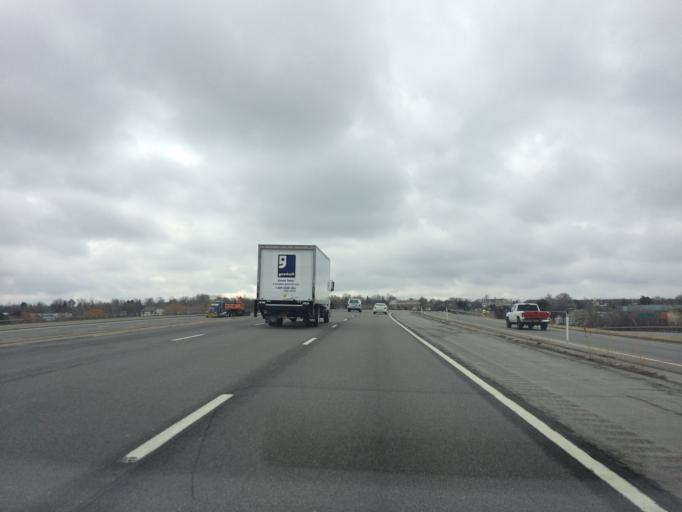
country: US
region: New York
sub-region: Monroe County
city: Rochester
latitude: 43.0894
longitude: -77.6040
